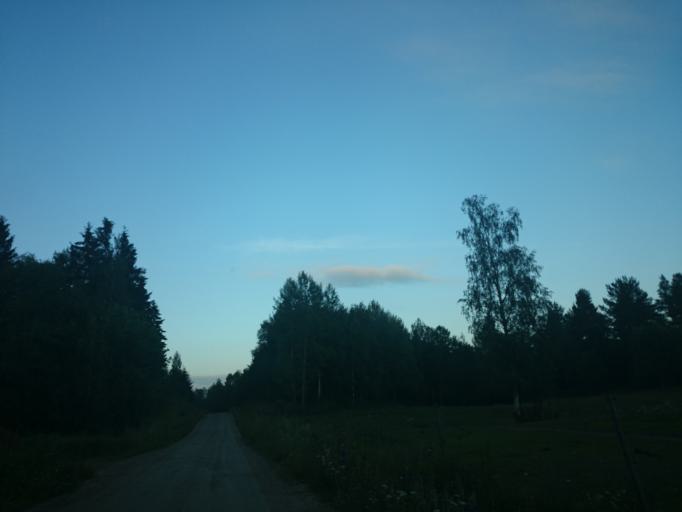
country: SE
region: Vaesternorrland
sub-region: Sundsvalls Kommun
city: Vi
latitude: 62.2067
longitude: 17.2521
